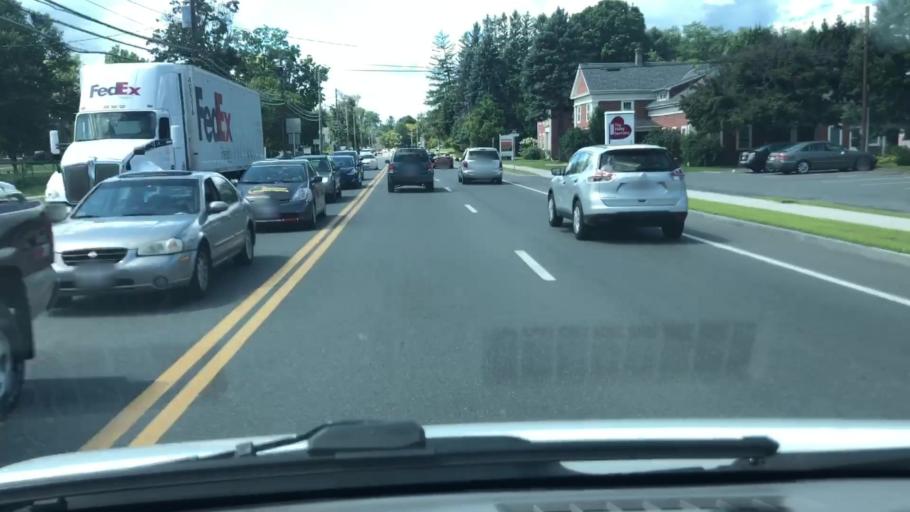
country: US
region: Massachusetts
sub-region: Hampshire County
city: Hadley
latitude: 42.3422
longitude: -72.5898
